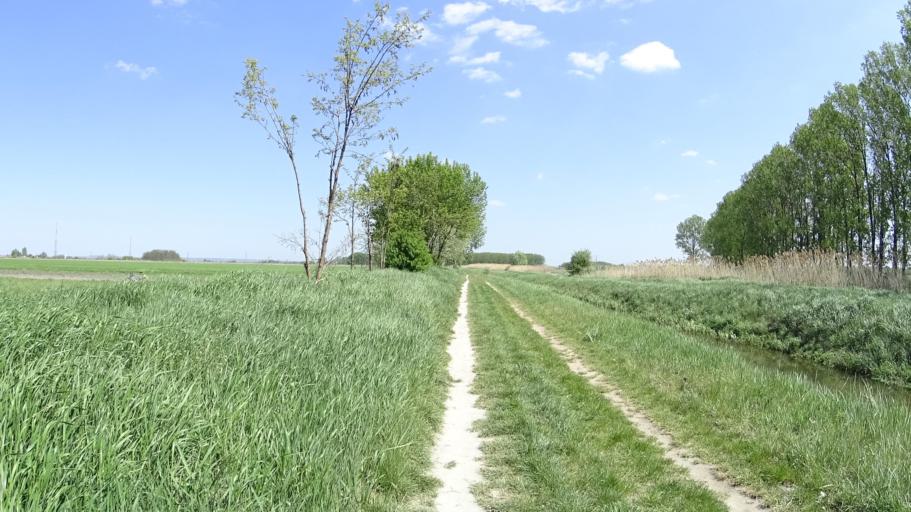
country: HU
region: Pest
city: Gyal
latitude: 47.3747
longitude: 19.2408
